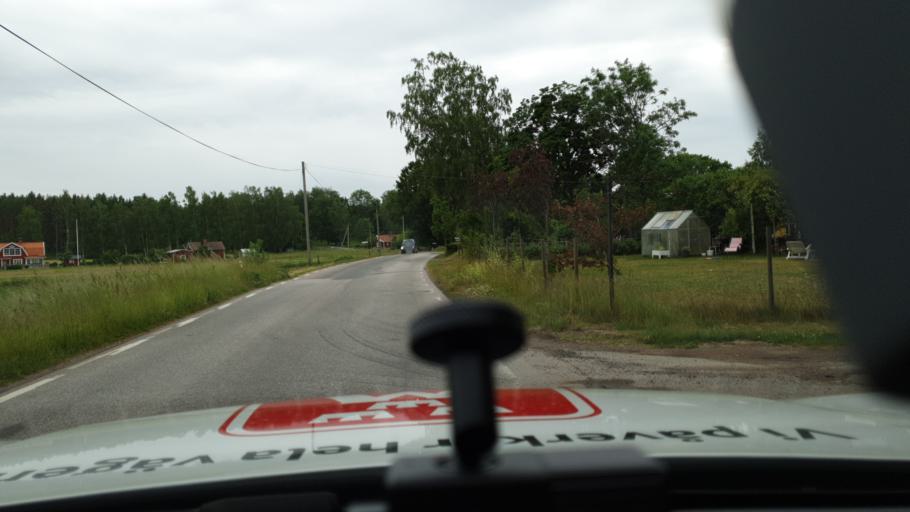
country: SE
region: Vaestra Goetaland
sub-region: Skovde Kommun
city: Stopen
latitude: 58.4909
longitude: 13.8703
